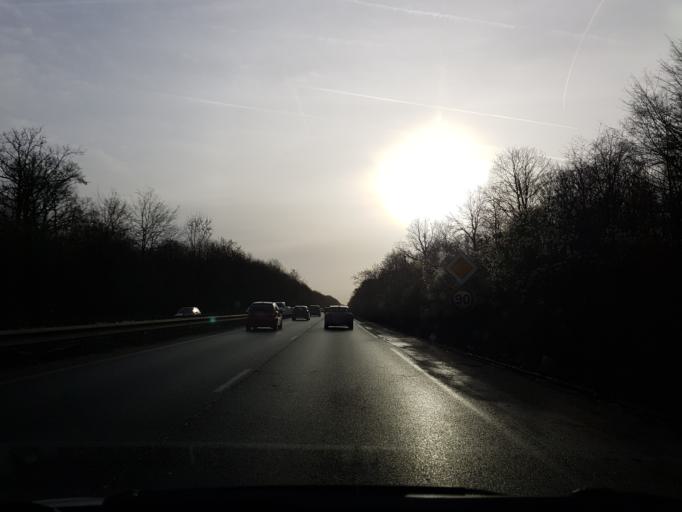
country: FR
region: Ile-de-France
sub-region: Departement de l'Essonne
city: Brunoy
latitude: 48.6772
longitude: 2.4975
